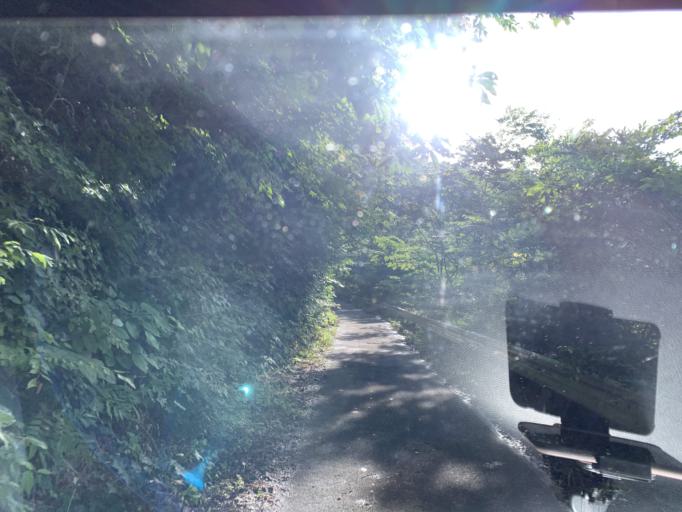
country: JP
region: Iwate
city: Ichinoseki
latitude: 38.9034
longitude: 140.9249
